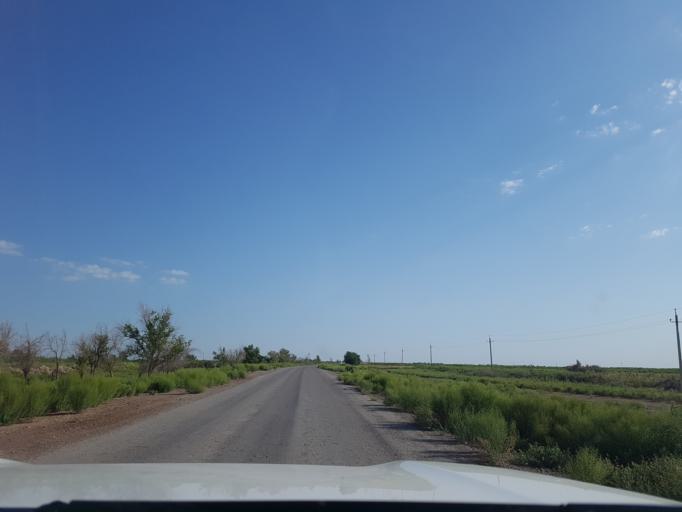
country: TM
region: Dasoguz
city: Koeneuergench
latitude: 41.8962
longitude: 58.7073
